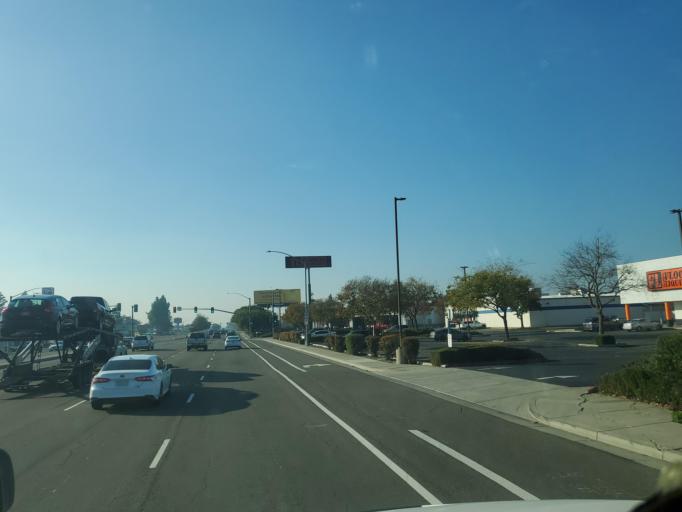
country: US
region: California
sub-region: San Joaquin County
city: Morada
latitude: 38.0213
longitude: -121.2664
